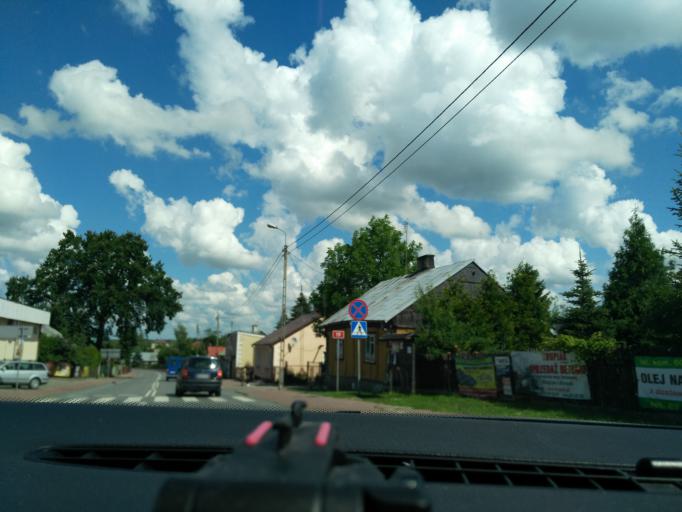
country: PL
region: Masovian Voivodeship
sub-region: Powiat losicki
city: Sarnaki
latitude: 52.3149
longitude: 22.8893
